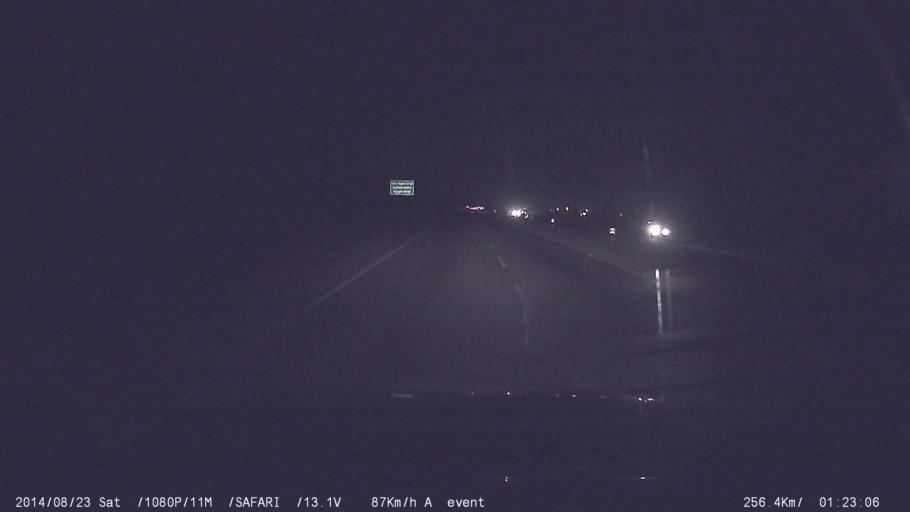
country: IN
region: Tamil Nadu
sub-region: Kancheepuram
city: Kanchipuram
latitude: 12.8729
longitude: 79.6329
